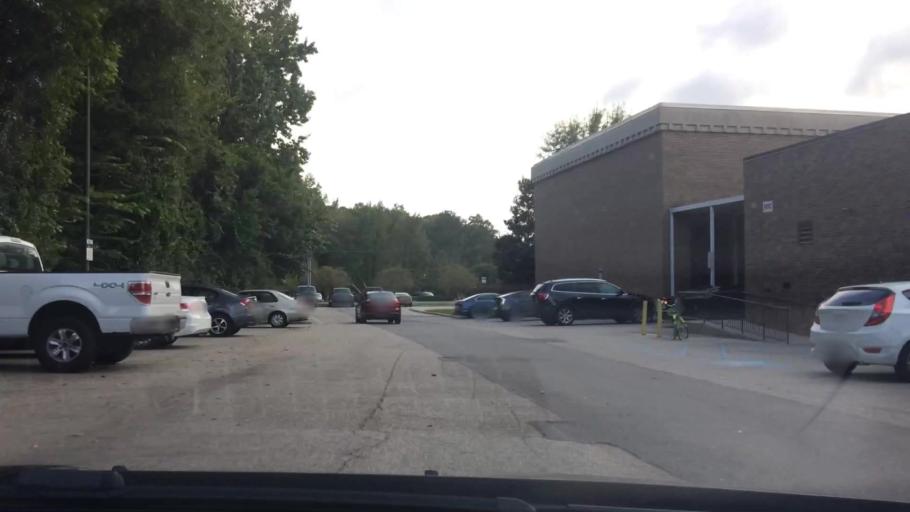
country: US
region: North Carolina
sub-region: Pitt County
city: Greenville
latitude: 35.6047
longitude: -77.3610
